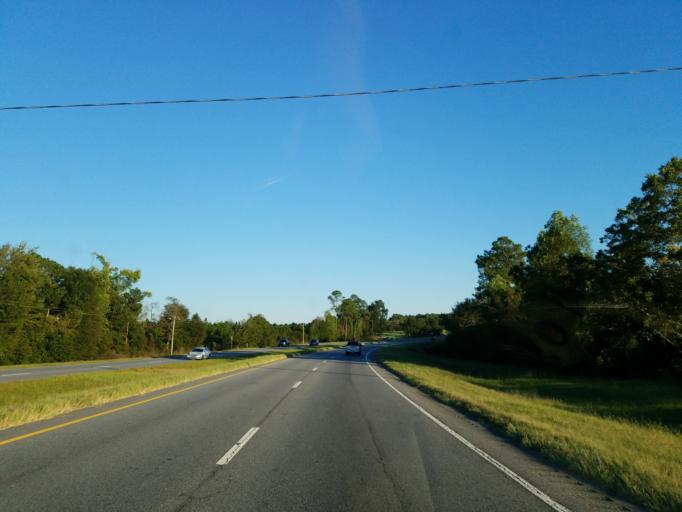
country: US
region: Georgia
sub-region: Worth County
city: Sylvester
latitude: 31.4965
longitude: -83.7100
